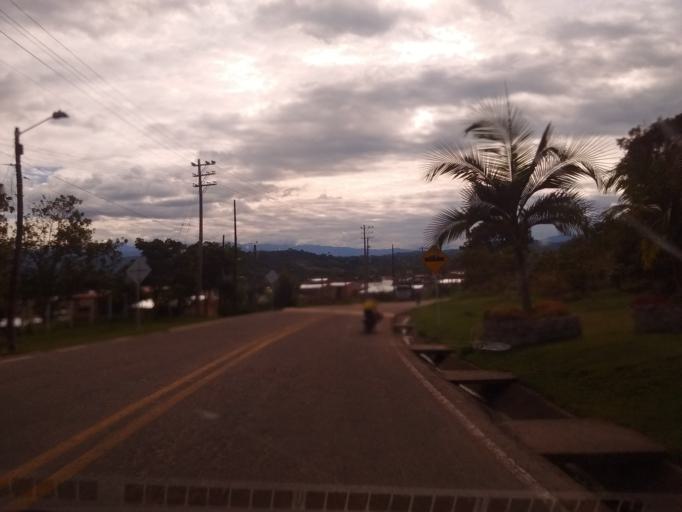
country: CO
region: Huila
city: San Agustin
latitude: 1.8760
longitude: -76.2614
